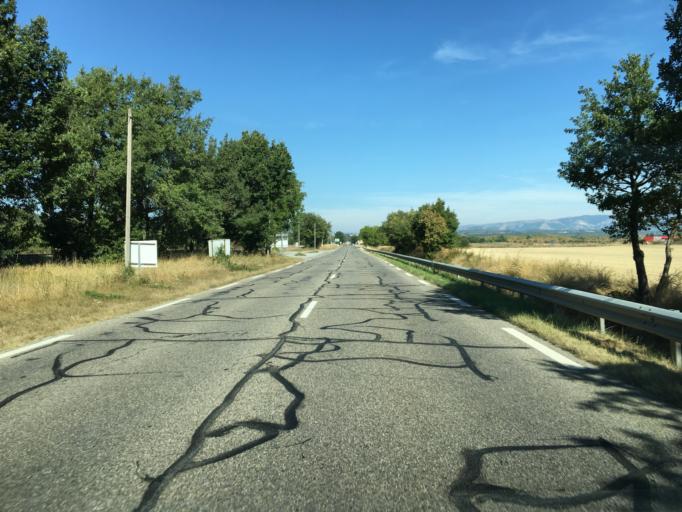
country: FR
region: Provence-Alpes-Cote d'Azur
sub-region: Departement des Alpes-de-Haute-Provence
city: Sisteron
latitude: 44.2289
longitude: 5.9087
